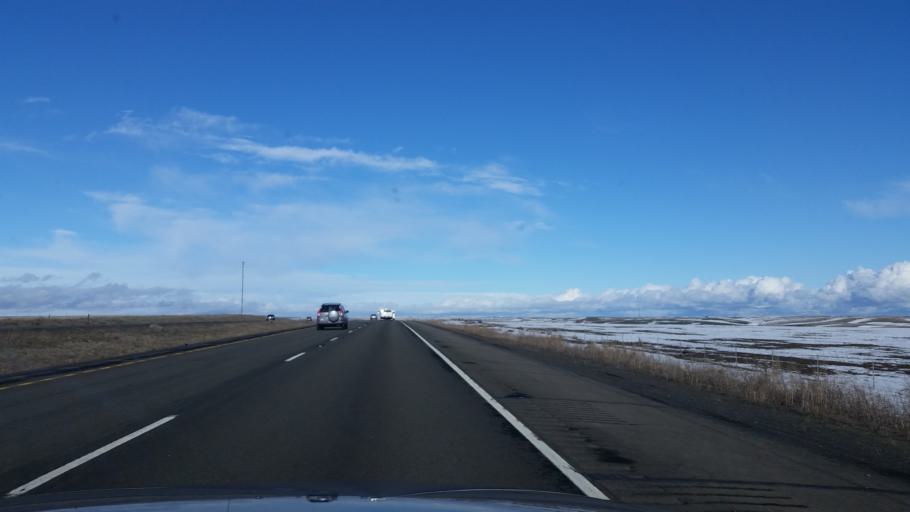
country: US
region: Washington
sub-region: Adams County
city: Ritzville
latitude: 47.1836
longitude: -118.2692
